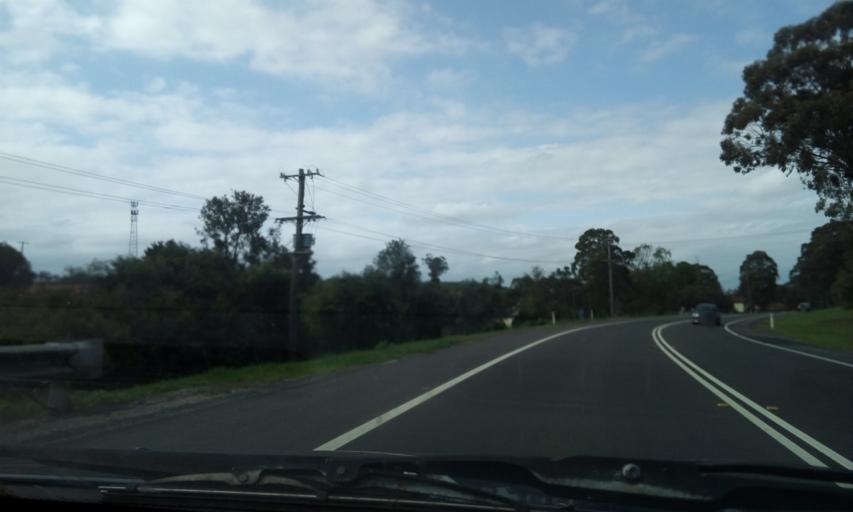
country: AU
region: New South Wales
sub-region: Campbelltown Municipality
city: Glen Alpine
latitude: -34.0853
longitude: 150.7742
